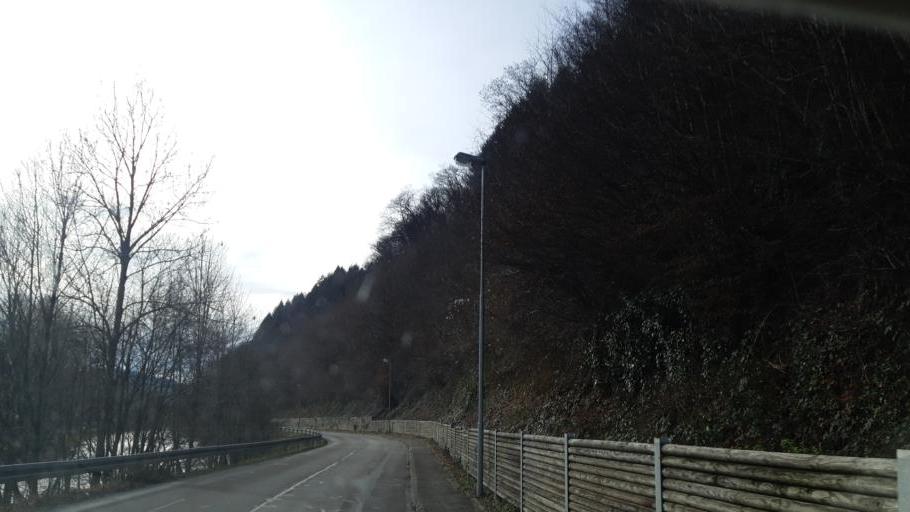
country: DE
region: Baden-Wuerttemberg
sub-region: Freiburg Region
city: Gutach im Breisgau
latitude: 48.1209
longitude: 7.9901
